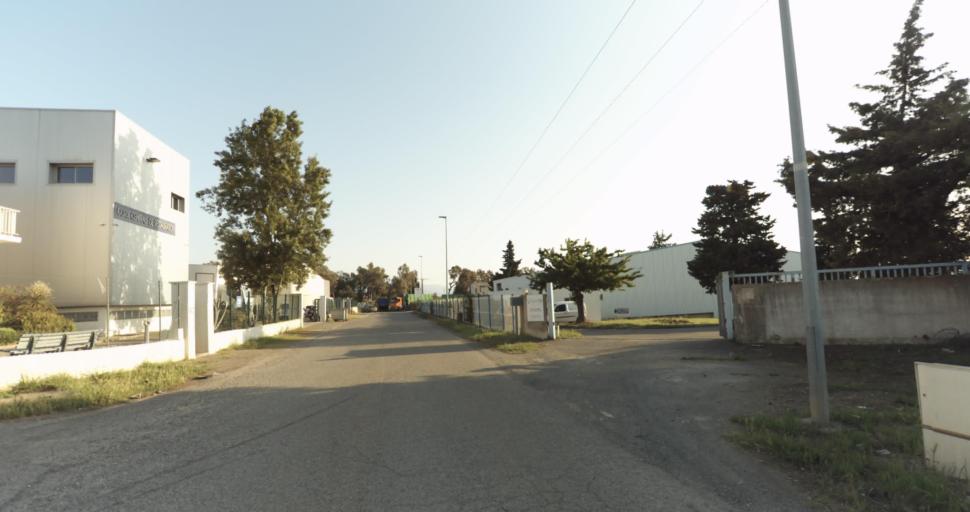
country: FR
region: Corsica
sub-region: Departement de la Haute-Corse
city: Biguglia
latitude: 42.5999
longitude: 9.4418
